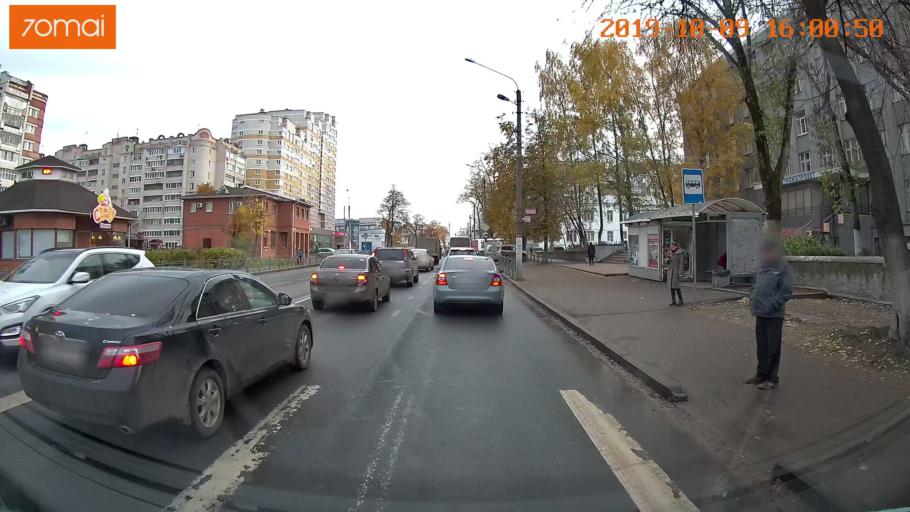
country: RU
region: Kostroma
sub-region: Kostromskoy Rayon
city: Kostroma
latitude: 57.7658
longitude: 40.9511
